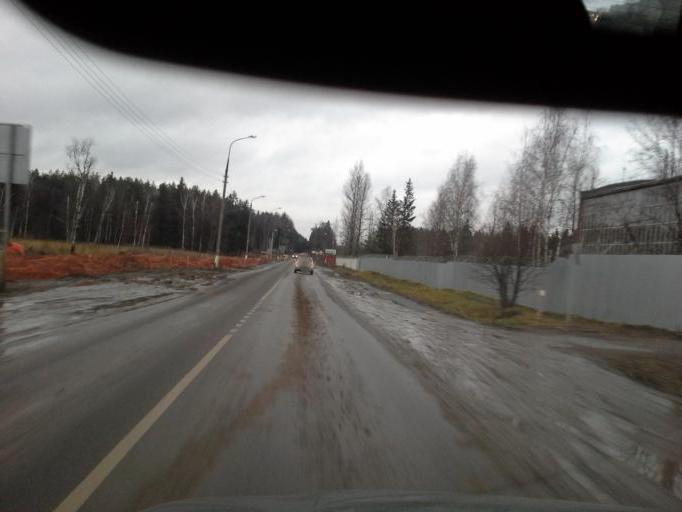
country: RU
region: Moskovskaya
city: Kokoshkino
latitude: 55.6027
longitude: 37.1640
